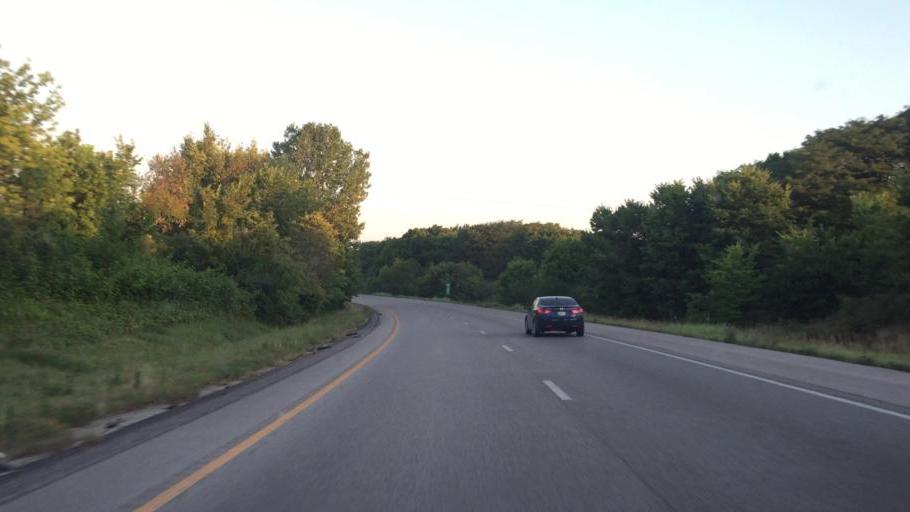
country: US
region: Missouri
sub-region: Clay County
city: Pleasant Valley
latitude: 39.3106
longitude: -94.5148
